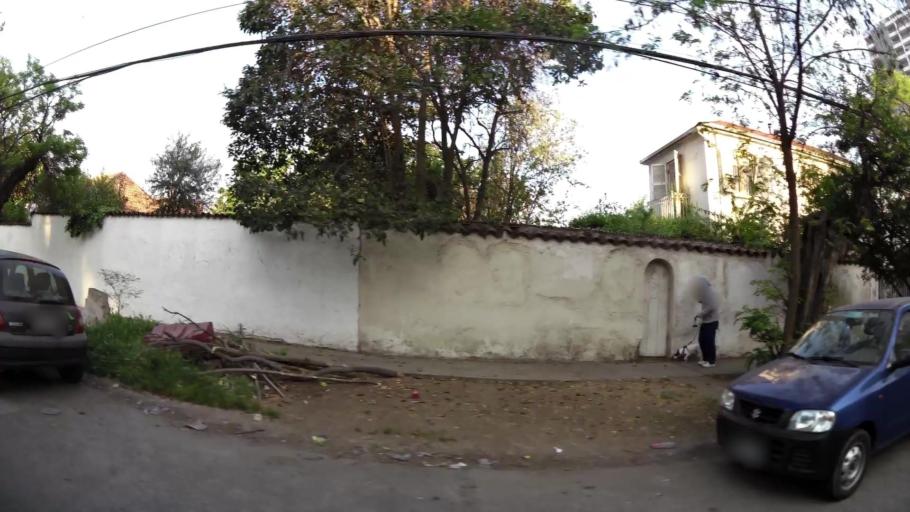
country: CL
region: Santiago Metropolitan
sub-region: Provincia de Santiago
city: Villa Presidente Frei, Nunoa, Santiago, Chile
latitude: -33.4557
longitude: -70.5766
